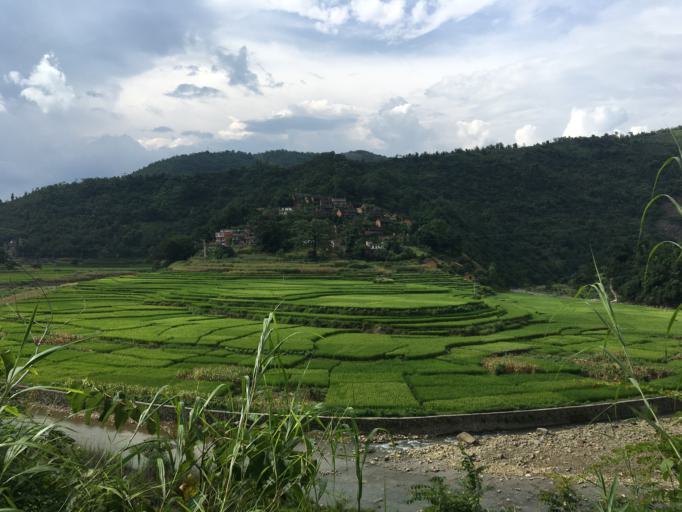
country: CN
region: Guangxi Zhuangzu Zizhiqu
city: Xinzhou
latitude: 24.7751
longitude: 105.8382
